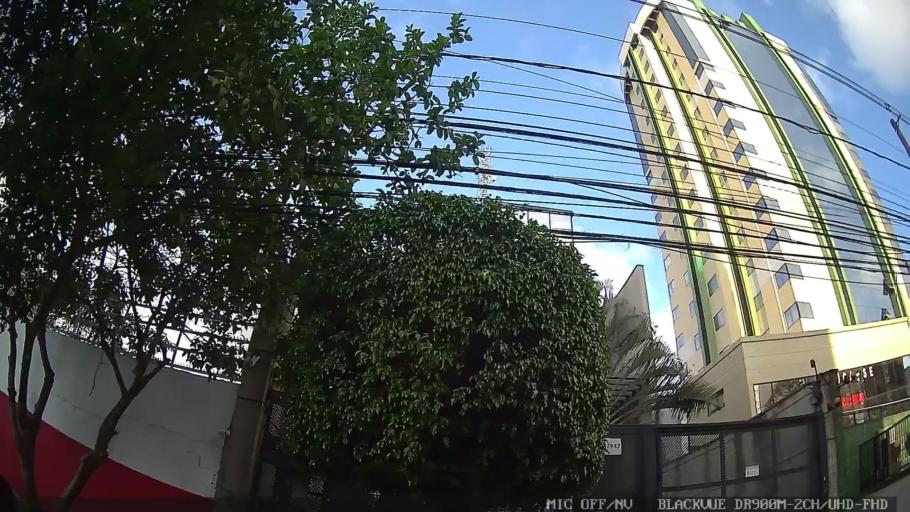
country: BR
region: Sao Paulo
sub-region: Sao Paulo
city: Sao Paulo
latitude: -23.5455
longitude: -46.5583
